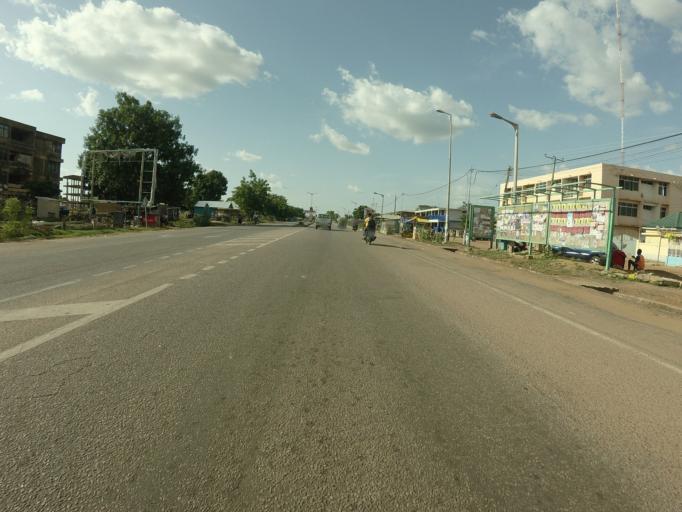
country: GH
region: Upper East
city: Bolgatanga
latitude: 10.7727
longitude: -0.8561
